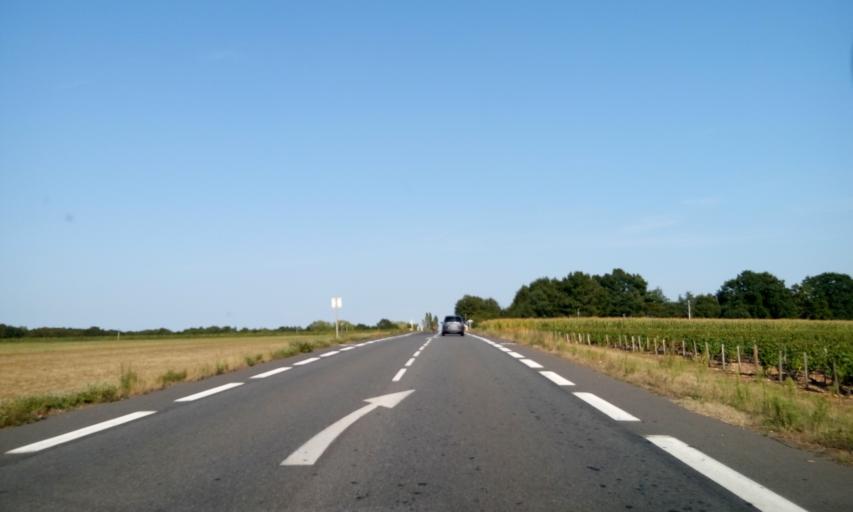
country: FR
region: Rhone-Alpes
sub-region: Departement du Rhone
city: Theize
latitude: 45.9259
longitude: 4.6356
